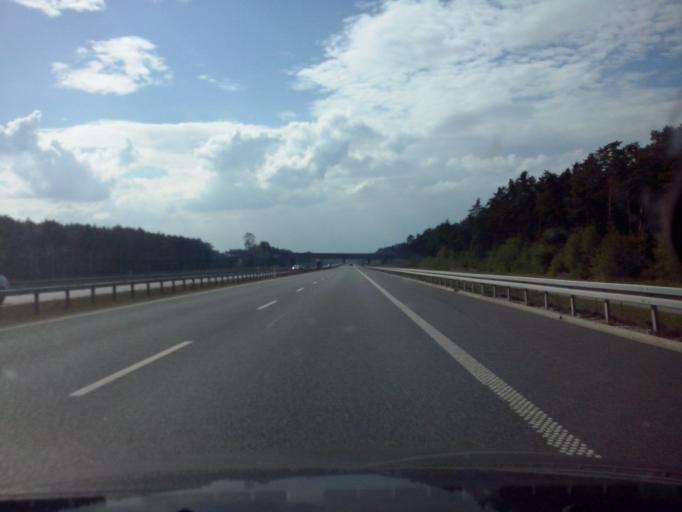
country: PL
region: Lesser Poland Voivodeship
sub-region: Powiat tarnowski
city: Wierzchoslawice
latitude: 50.0073
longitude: 20.8266
